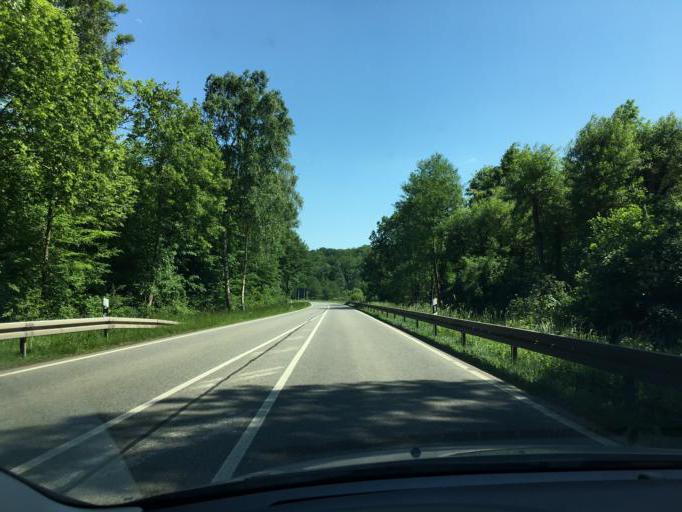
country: DE
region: Hesse
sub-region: Regierungsbezirk Kassel
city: Ronshausen
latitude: 50.9434
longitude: 9.8905
